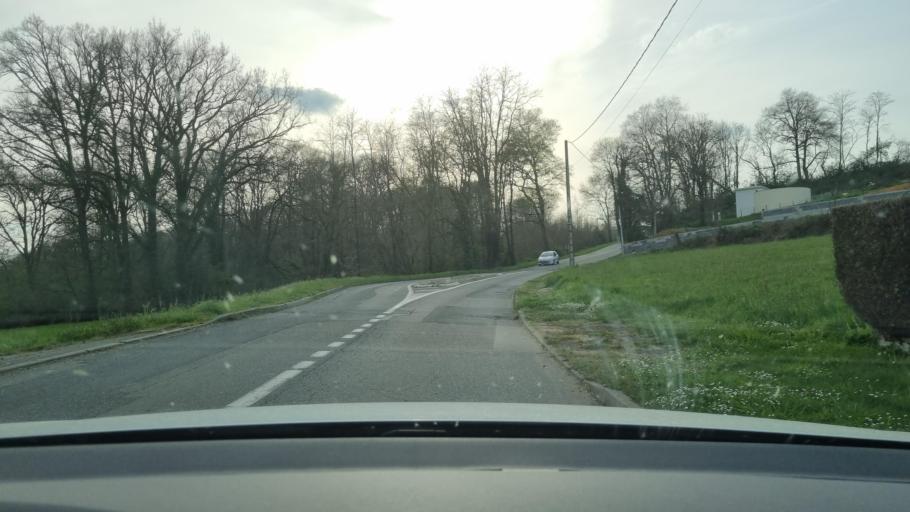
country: FR
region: Aquitaine
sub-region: Departement des Pyrenees-Atlantiques
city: Soumoulou
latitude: 43.3777
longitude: -0.1355
